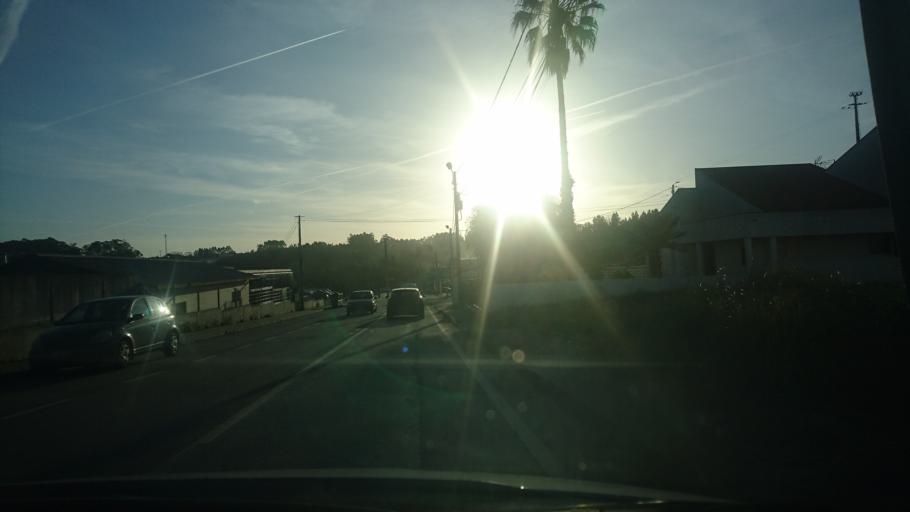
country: PT
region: Aveiro
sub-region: Santa Maria da Feira
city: Pacos de Brandao
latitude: 40.9800
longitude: -8.6015
